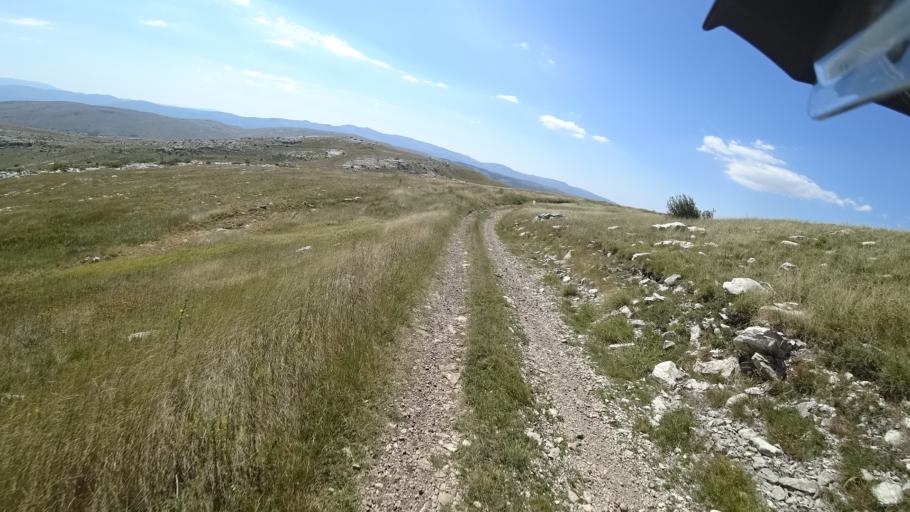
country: HR
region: Splitsko-Dalmatinska
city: Hrvace
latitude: 43.8862
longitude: 16.6410
